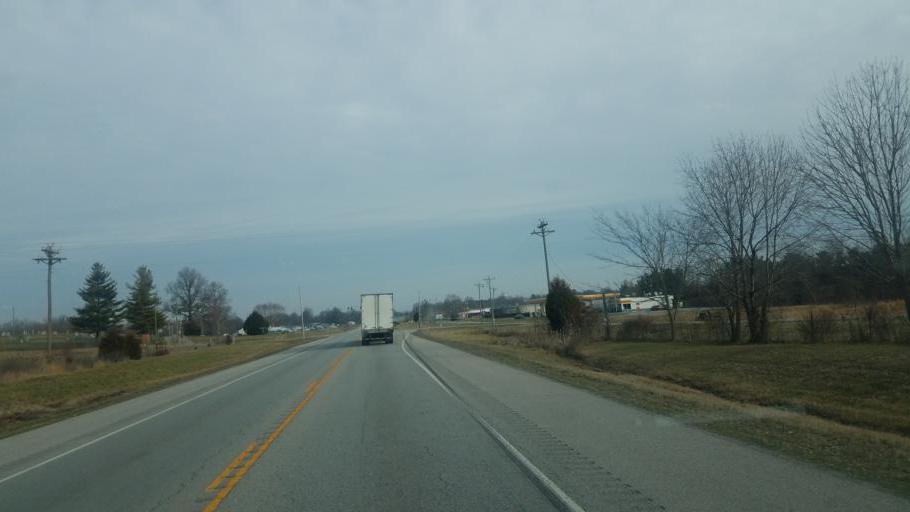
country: US
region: Kentucky
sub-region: Boyle County
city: Junction City
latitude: 37.5745
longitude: -84.7925
